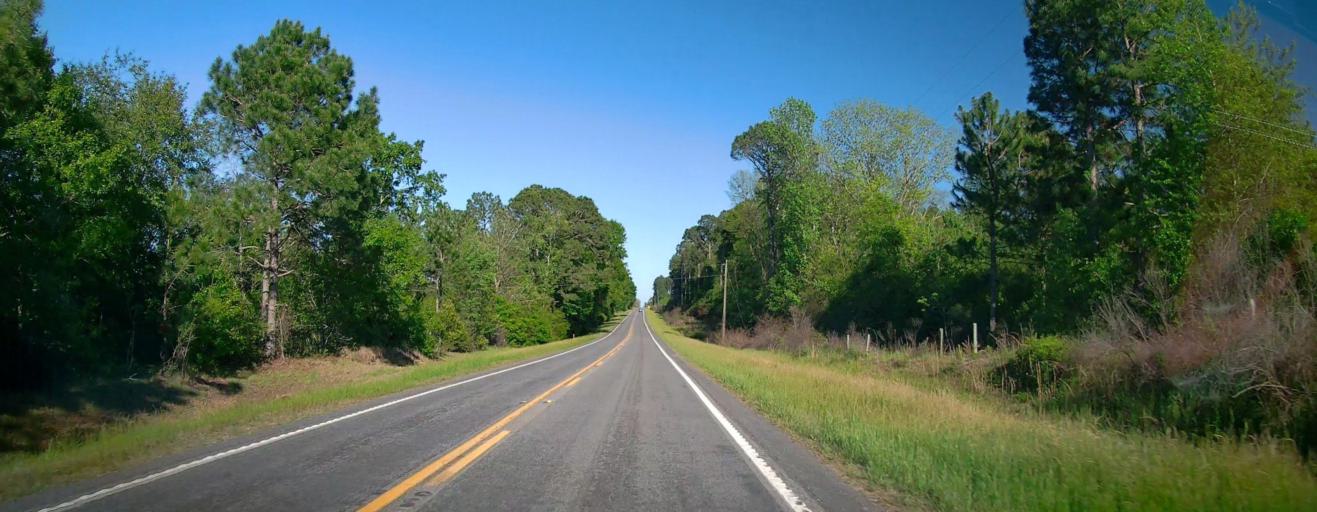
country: US
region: Georgia
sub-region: Ben Hill County
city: Fitzgerald
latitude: 31.7188
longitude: -83.3487
